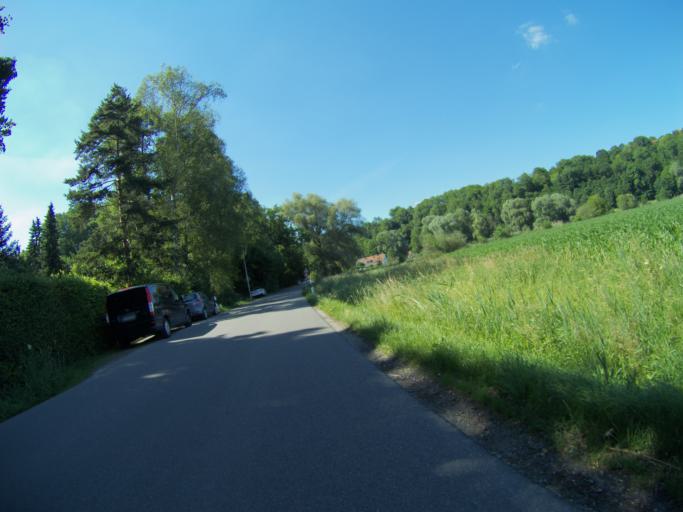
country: DE
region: Bavaria
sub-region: Upper Bavaria
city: Freising
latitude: 48.3918
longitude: 11.7252
